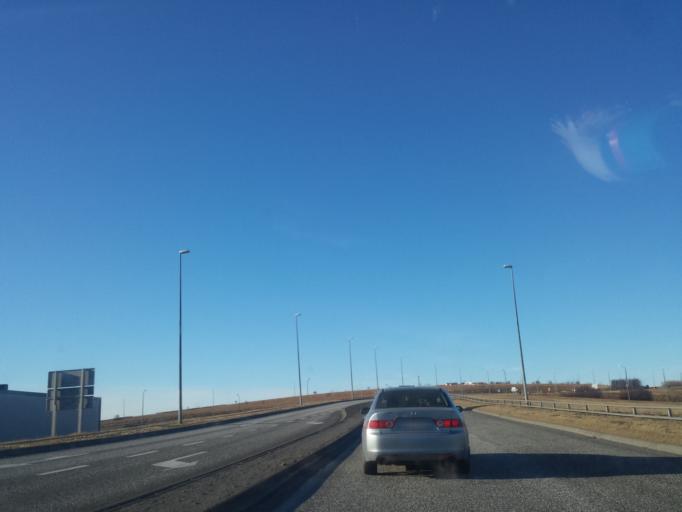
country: IS
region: Capital Region
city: Mosfellsbaer
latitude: 64.1316
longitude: -21.7612
